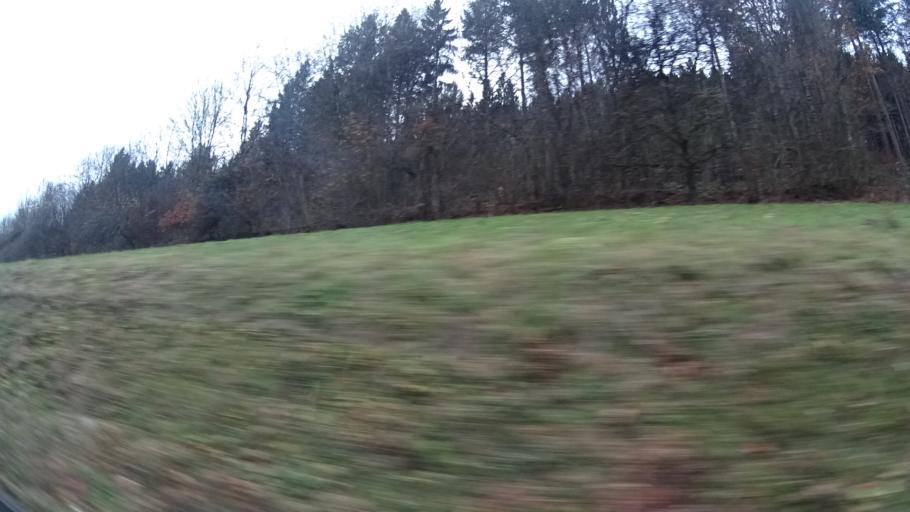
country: DE
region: Baden-Wuerttemberg
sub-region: Karlsruhe Region
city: Eberbach
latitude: 49.4455
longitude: 8.9559
